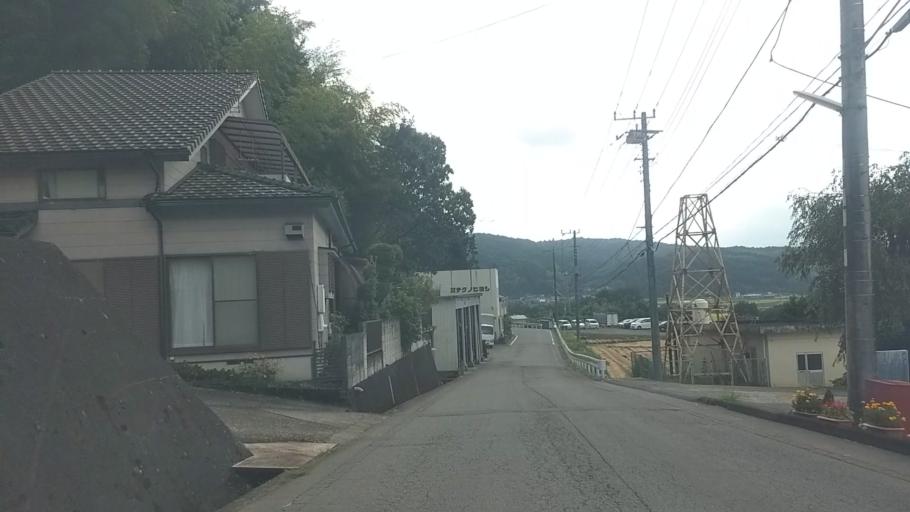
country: JP
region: Shizuoka
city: Ito
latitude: 34.9741
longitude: 138.9760
